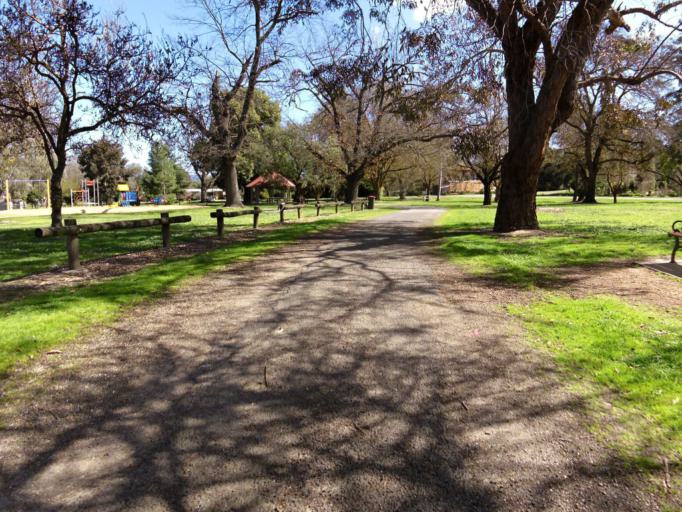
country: AU
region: Victoria
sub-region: Murrindindi
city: Alexandra
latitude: -37.1880
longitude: 145.7115
